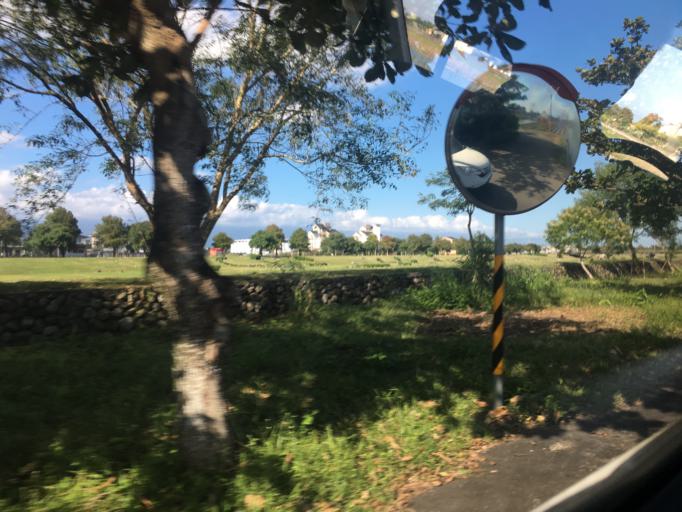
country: TW
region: Taiwan
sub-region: Yilan
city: Yilan
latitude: 24.6938
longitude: 121.7429
